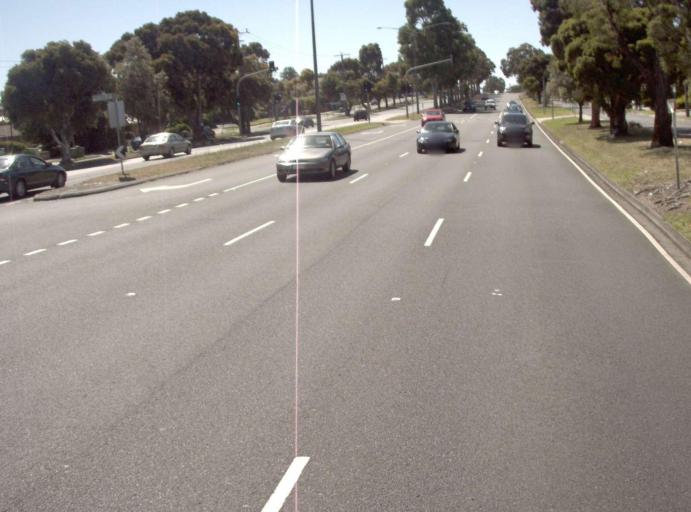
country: AU
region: Victoria
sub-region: Greater Dandenong
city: Dandenong
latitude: -37.9783
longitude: 145.2072
